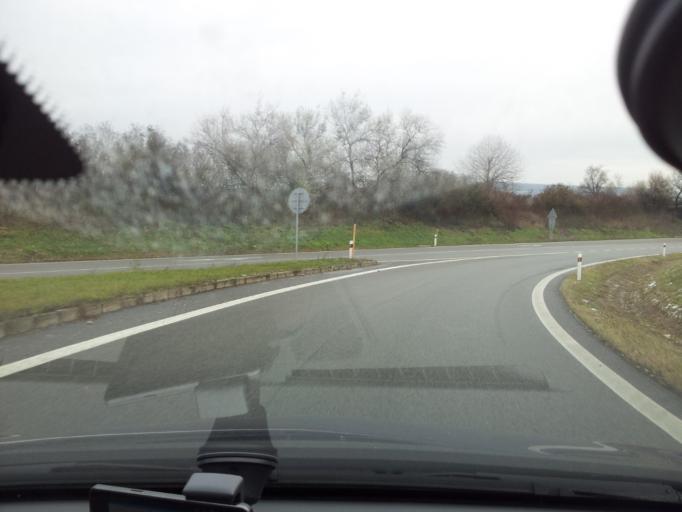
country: SK
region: Kosicky
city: Kosice
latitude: 48.7889
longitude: 21.3081
